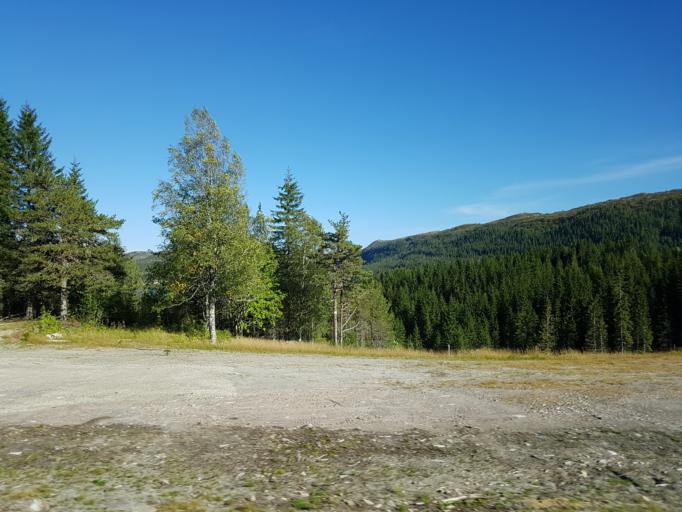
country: NO
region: Sor-Trondelag
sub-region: Afjord
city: A i Afjord
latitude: 63.7788
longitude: 10.2181
